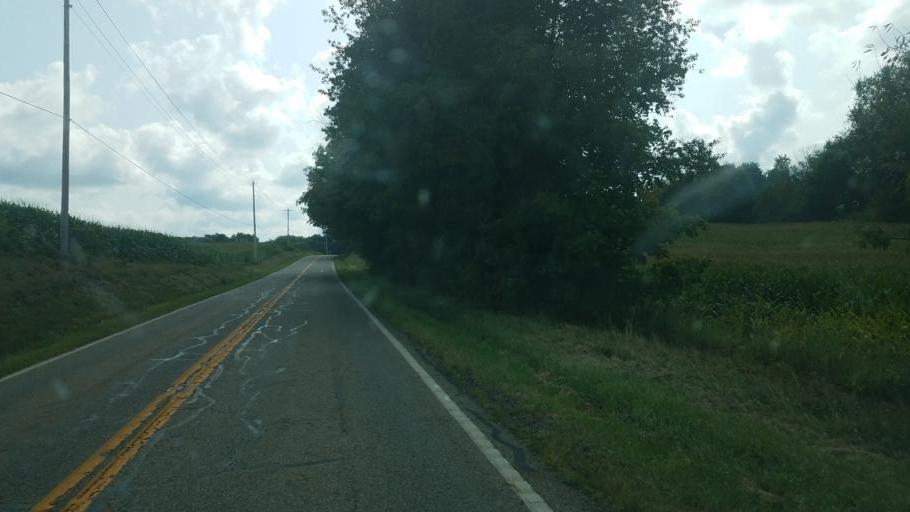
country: US
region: Ohio
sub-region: Stark County
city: Minerva
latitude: 40.7903
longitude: -81.0196
